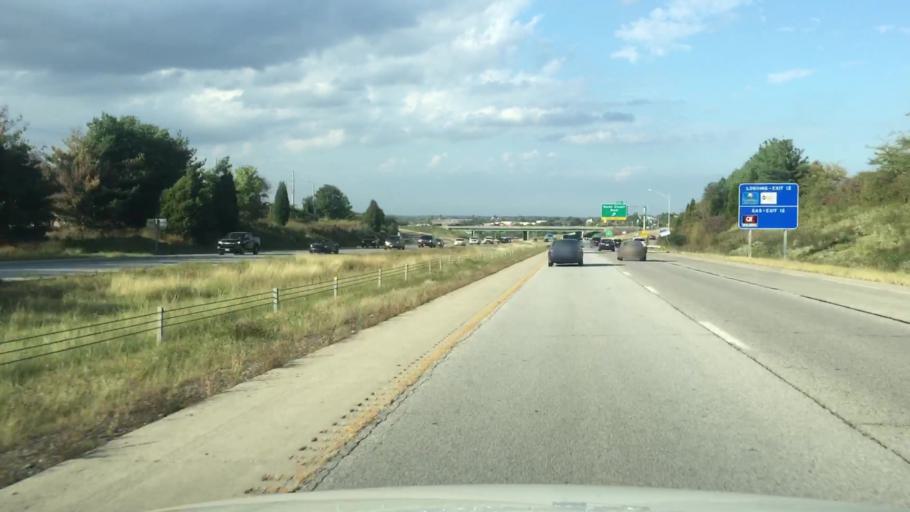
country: US
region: Missouri
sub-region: Jackson County
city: Lees Summit
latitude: 38.9783
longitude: -94.3565
